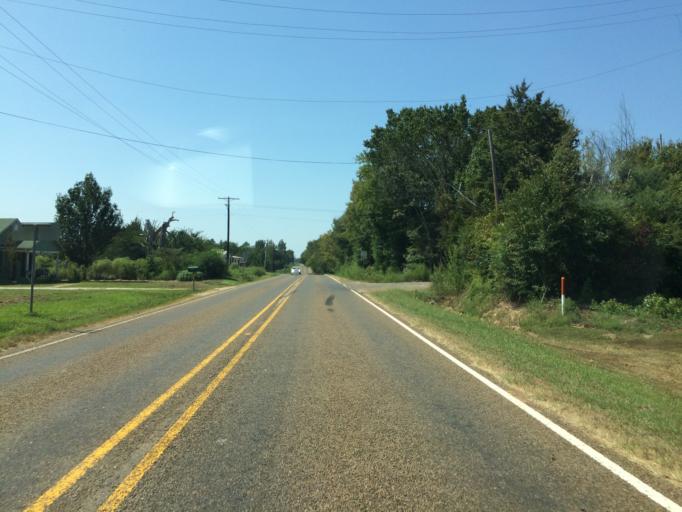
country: US
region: Texas
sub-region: Wood County
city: Quitman
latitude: 32.7173
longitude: -95.3676
